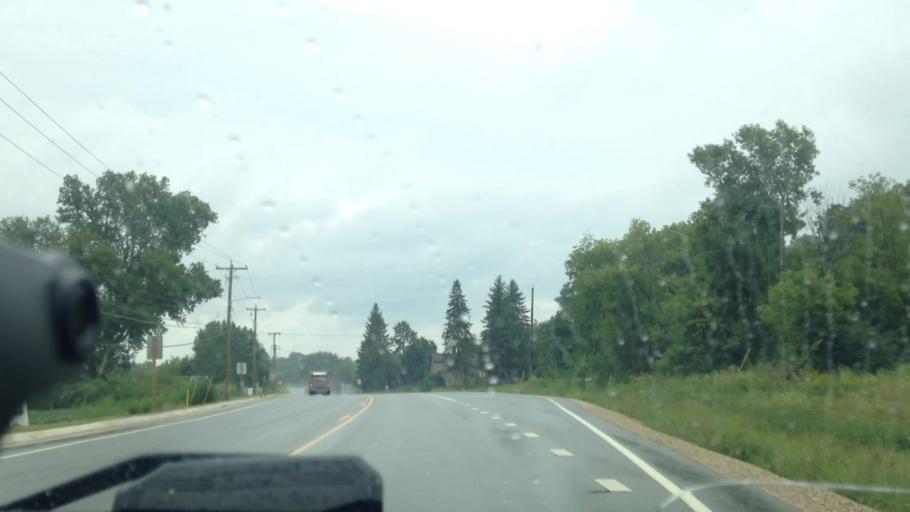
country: US
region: Wisconsin
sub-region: Washington County
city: Richfield
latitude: 43.2296
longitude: -88.1828
